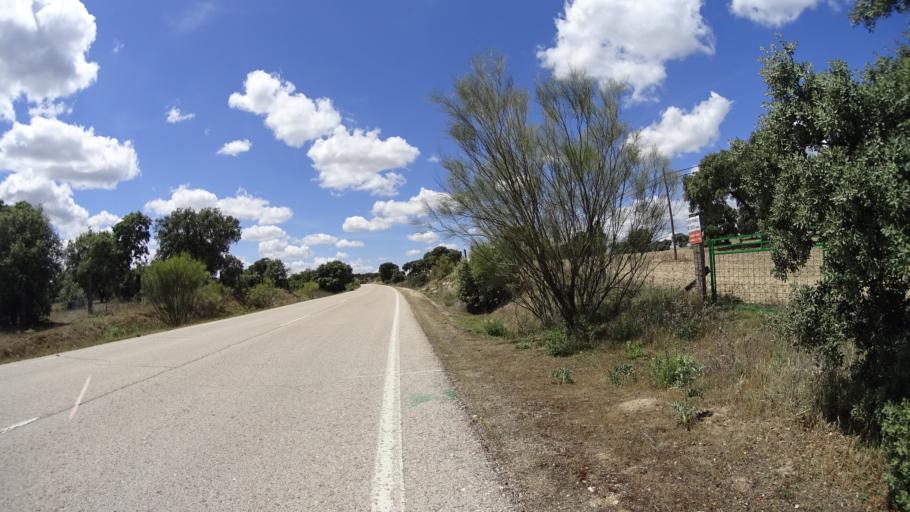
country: ES
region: Madrid
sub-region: Provincia de Madrid
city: Villanueva del Pardillo
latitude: 40.4552
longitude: -3.9502
